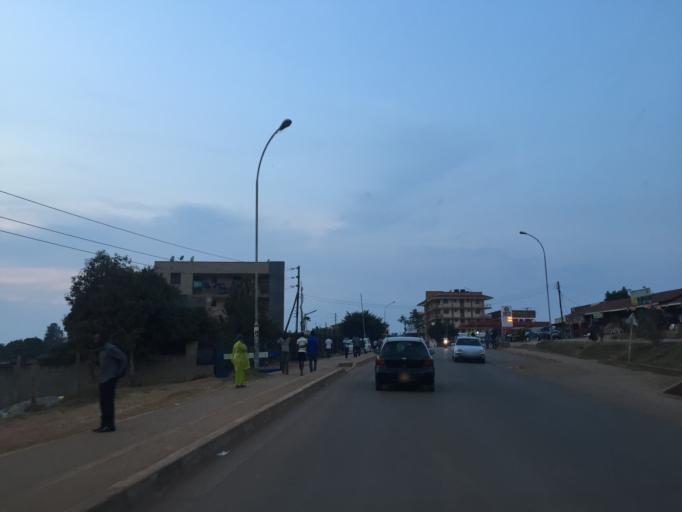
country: UG
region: Central Region
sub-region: Kampala District
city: Kampala
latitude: 0.2643
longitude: 32.6249
